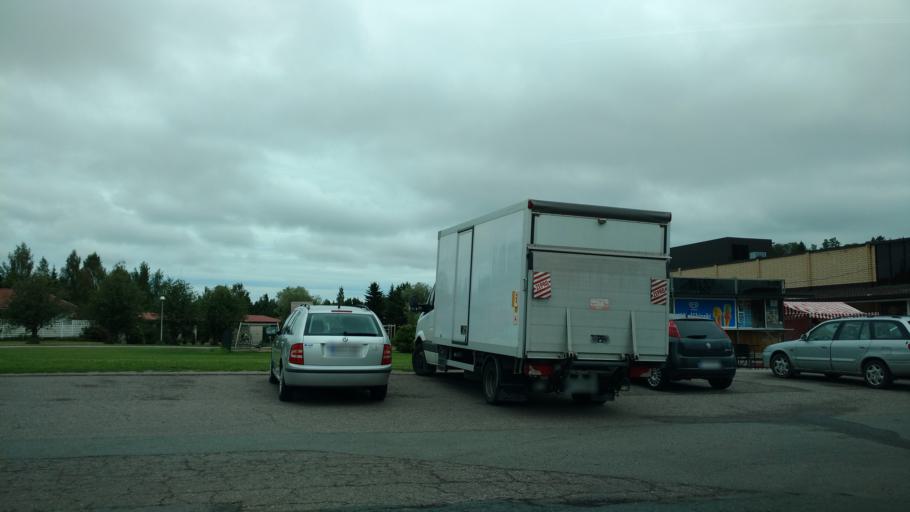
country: FI
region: Varsinais-Suomi
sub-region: Salo
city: Halikko
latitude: 60.3967
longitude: 23.0804
